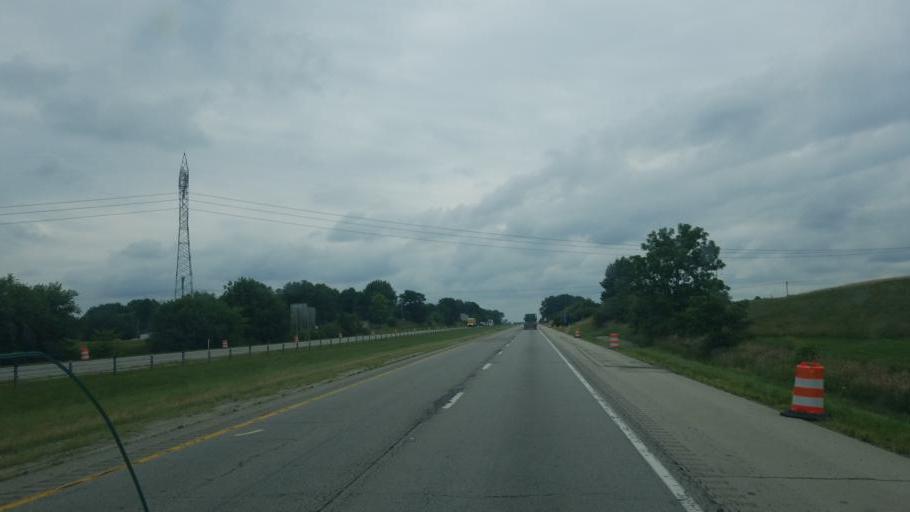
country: US
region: Indiana
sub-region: Madison County
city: Pendleton
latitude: 40.0410
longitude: -85.7101
